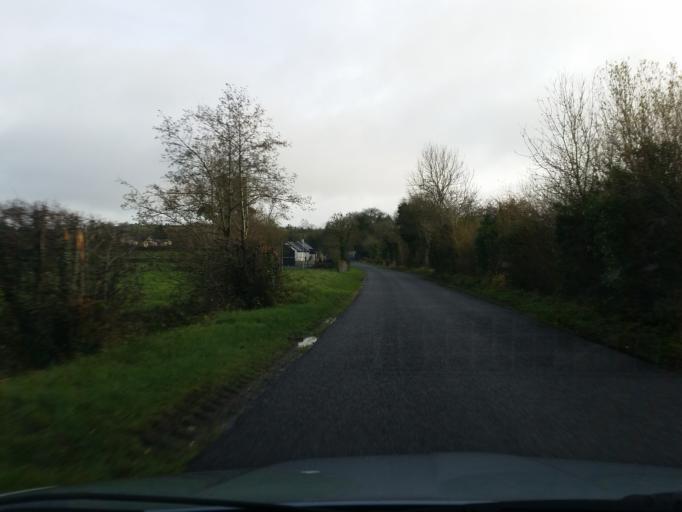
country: GB
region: Northern Ireland
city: Lisnaskea
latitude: 54.2410
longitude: -7.3745
